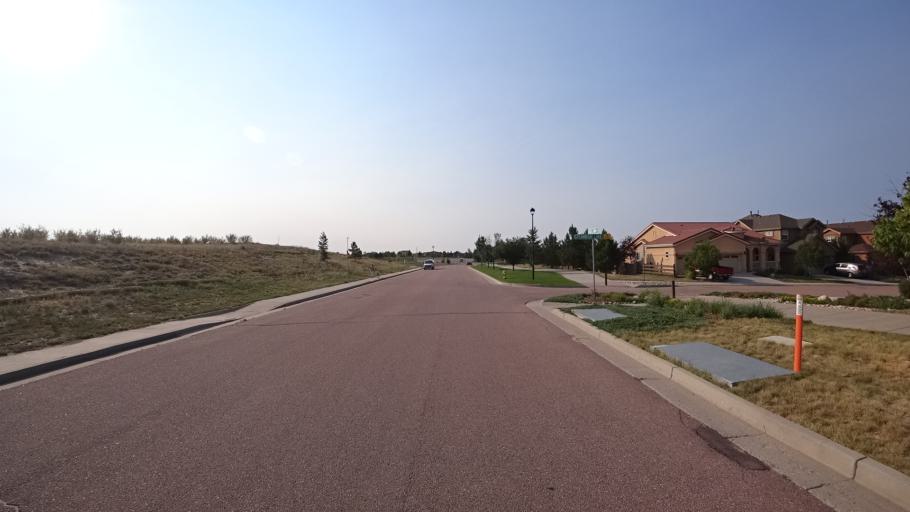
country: US
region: Colorado
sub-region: El Paso County
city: Black Forest
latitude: 38.9736
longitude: -104.7362
